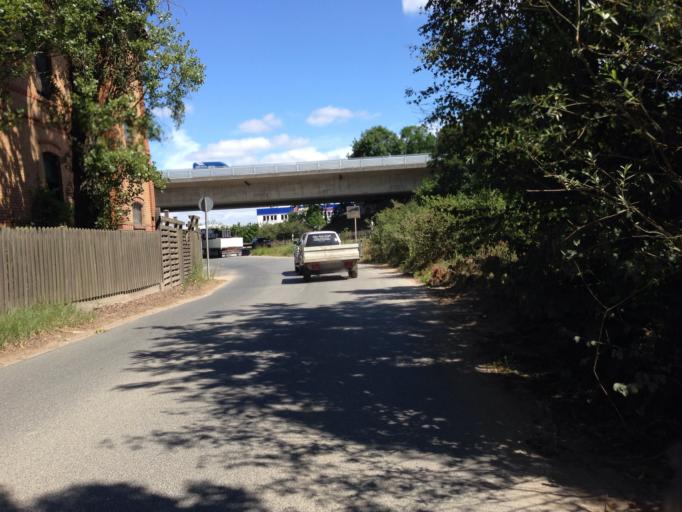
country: DE
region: Hesse
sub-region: Regierungsbezirk Darmstadt
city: Hanau am Main
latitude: 50.1166
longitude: 8.9428
